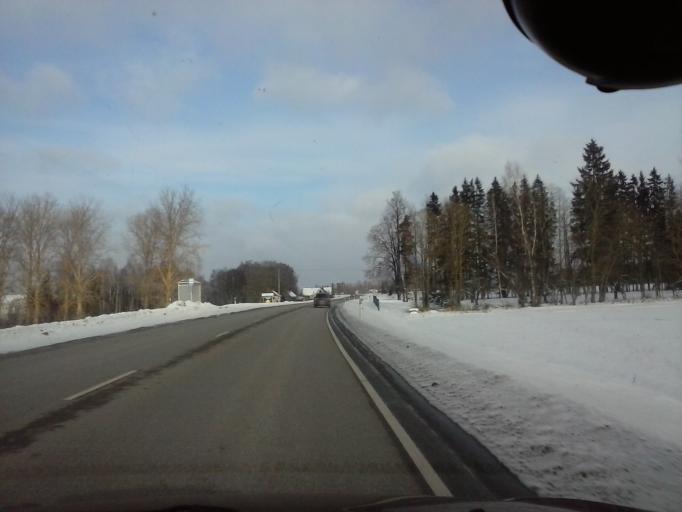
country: EE
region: Viljandimaa
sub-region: Viiratsi vald
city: Viiratsi
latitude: 58.3783
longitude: 25.6613
